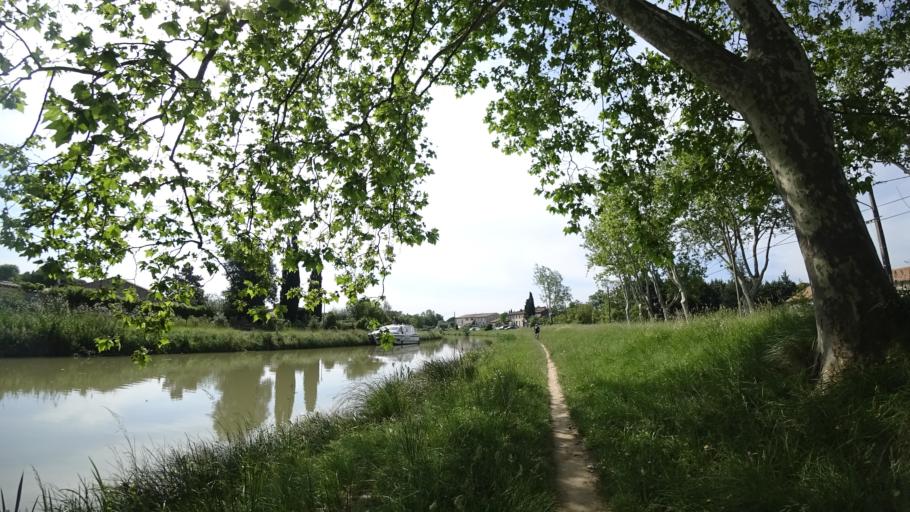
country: FR
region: Languedoc-Roussillon
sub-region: Departement de l'Aude
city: Lezignan-Corbieres
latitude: 43.2417
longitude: 2.7640
